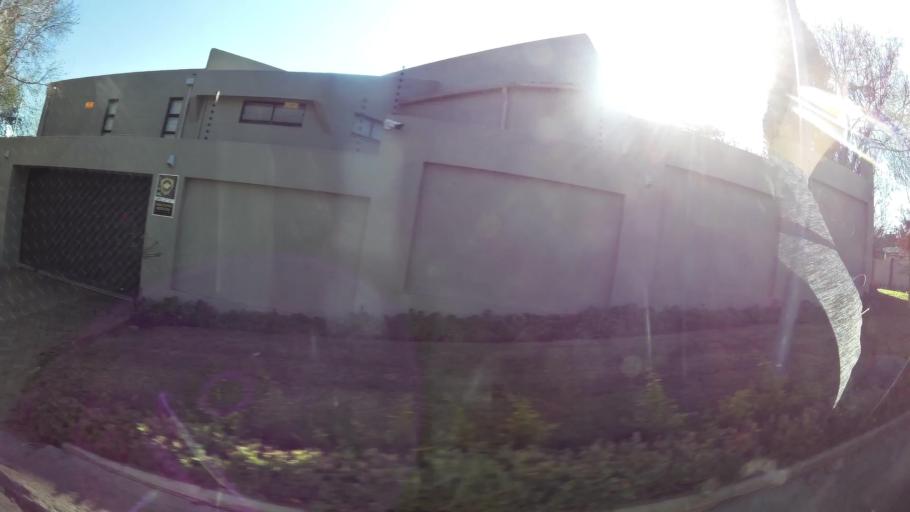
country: ZA
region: Gauteng
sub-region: City of Johannesburg Metropolitan Municipality
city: Midrand
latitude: -26.0719
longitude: 28.0400
